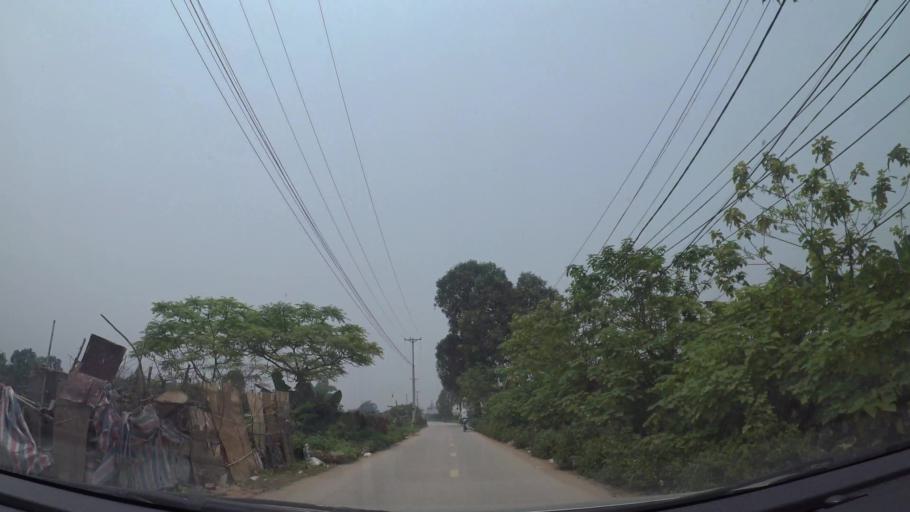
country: VN
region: Ha Noi
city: Ha Dong
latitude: 20.9967
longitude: 105.7700
